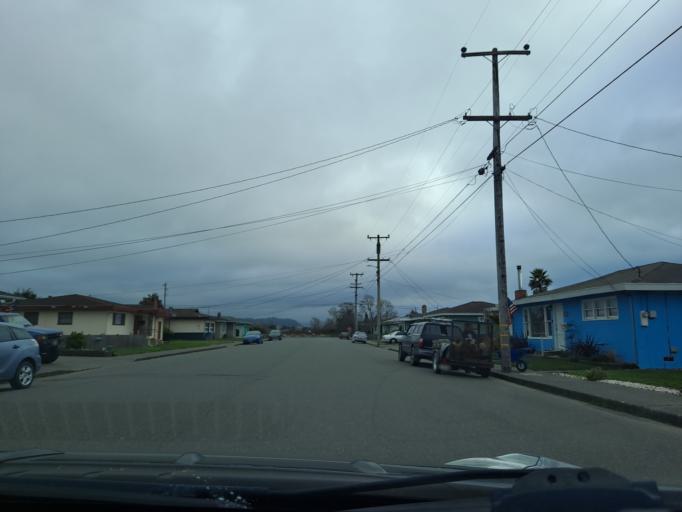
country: US
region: California
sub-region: Humboldt County
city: Fortuna
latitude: 40.5896
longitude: -124.1514
